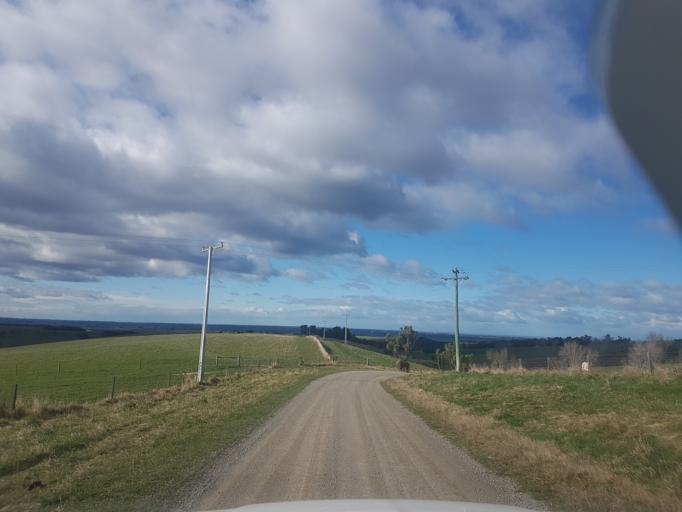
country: NZ
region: Canterbury
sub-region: Timaru District
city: Pleasant Point
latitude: -44.1828
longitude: 171.1266
